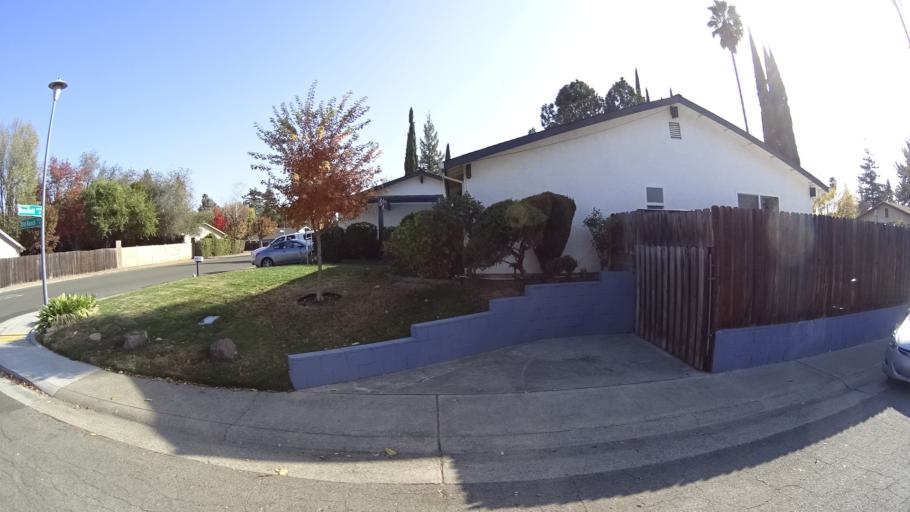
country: US
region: California
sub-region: Sacramento County
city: Orangevale
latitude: 38.6959
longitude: -121.2490
